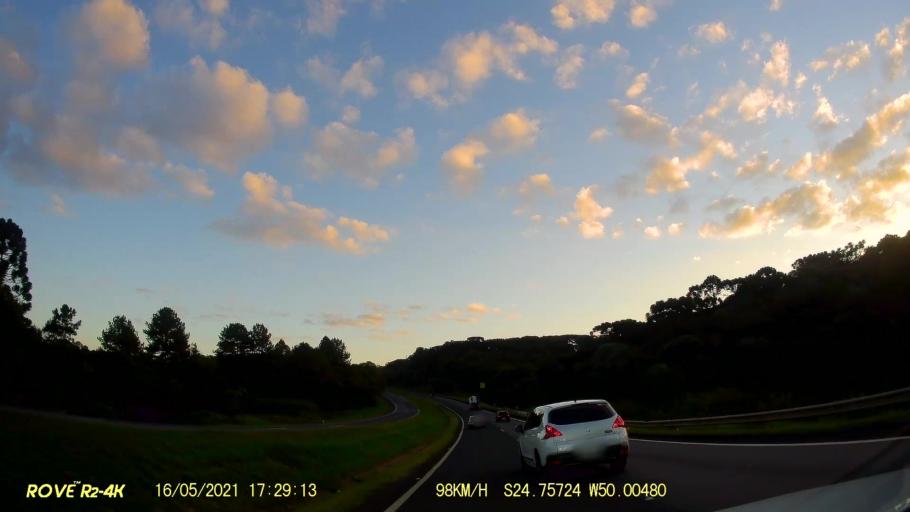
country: BR
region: Parana
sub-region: Castro
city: Castro
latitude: -24.7569
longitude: -50.0047
